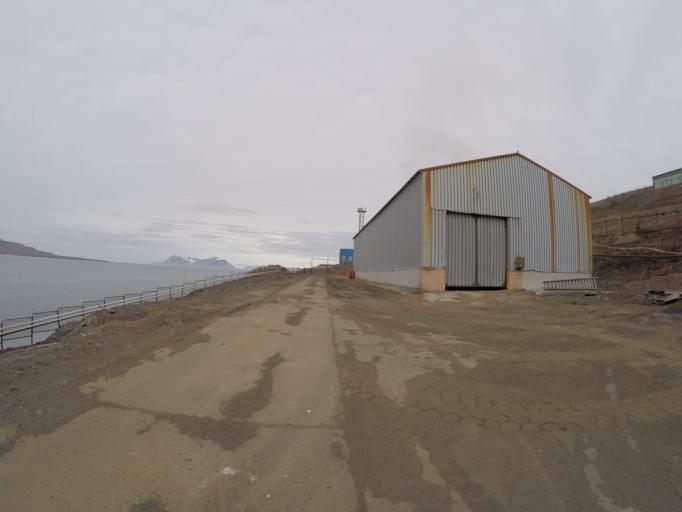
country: SJ
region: Svalbard
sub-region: Spitsbergen
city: Longyearbyen
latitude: 78.0528
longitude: 14.2123
